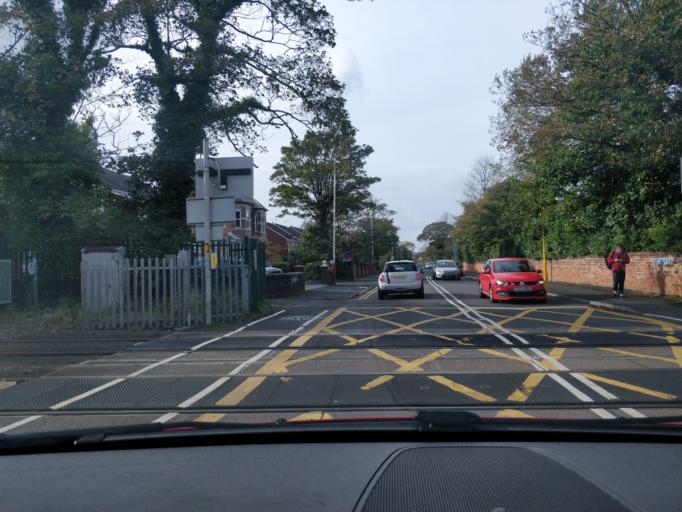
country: GB
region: England
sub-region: Sefton
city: Southport
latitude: 53.6293
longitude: -3.0184
